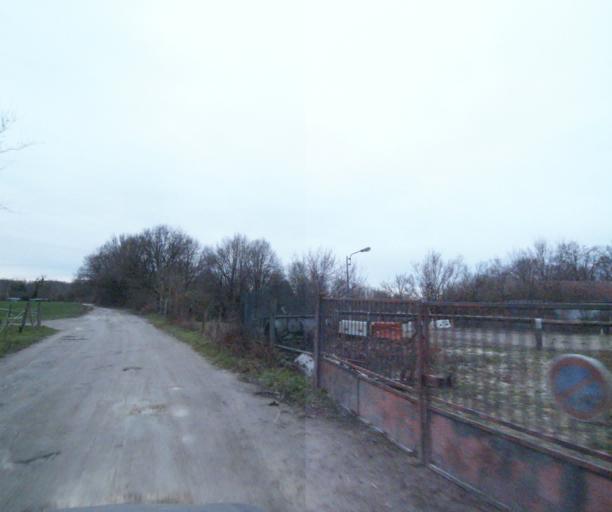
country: FR
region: Ile-de-France
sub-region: Departement de Seine-et-Marne
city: Longperrier
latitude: 49.0612
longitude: 2.6611
